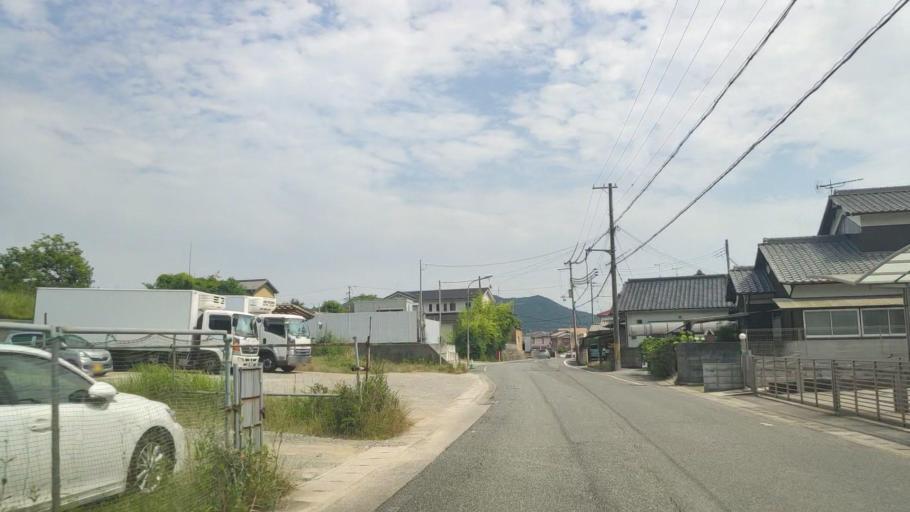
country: JP
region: Hyogo
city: Tatsunocho-tominaga
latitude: 34.8372
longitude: 134.6021
